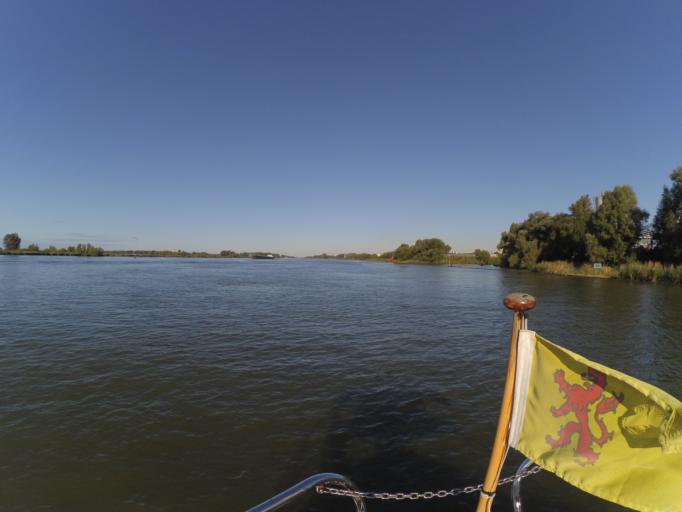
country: NL
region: South Holland
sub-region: Gemeente Zwijndrecht
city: Zwijndrecht
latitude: 51.8033
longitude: 4.6137
